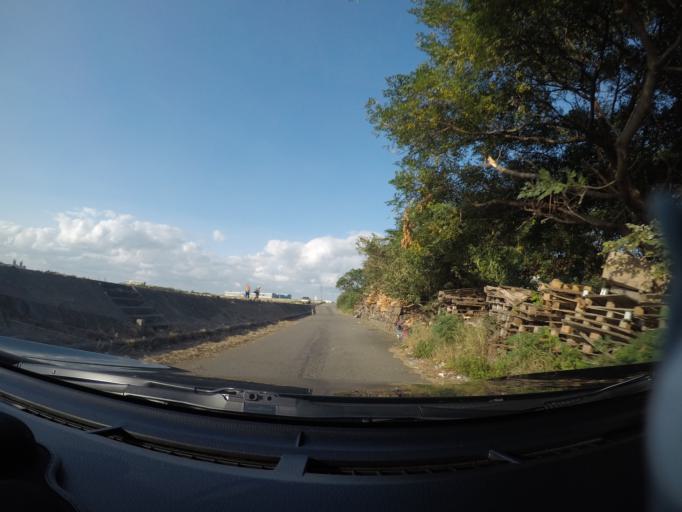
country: TW
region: Taiwan
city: Taoyuan City
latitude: 25.1007
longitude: 121.2517
